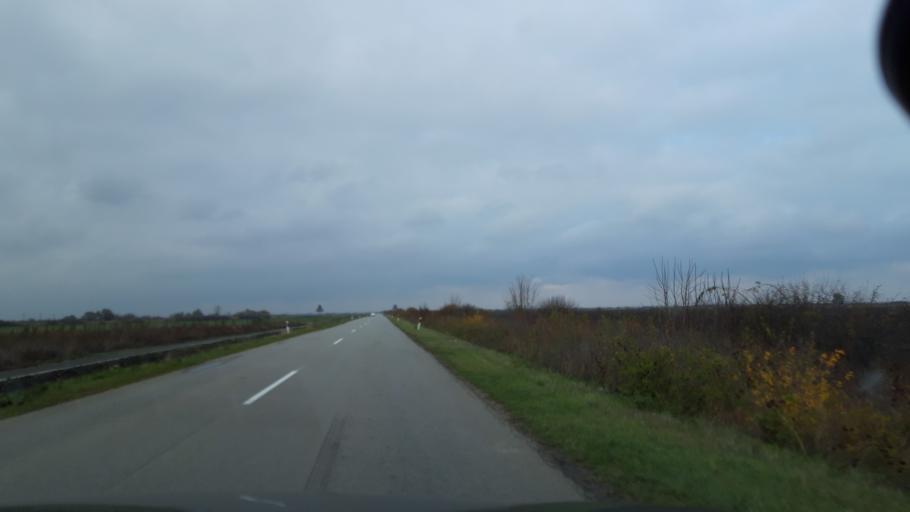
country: RS
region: Autonomna Pokrajina Vojvodina
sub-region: Severnobanatski Okrug
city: Novi Knezevac
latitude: 46.0820
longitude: 20.1058
